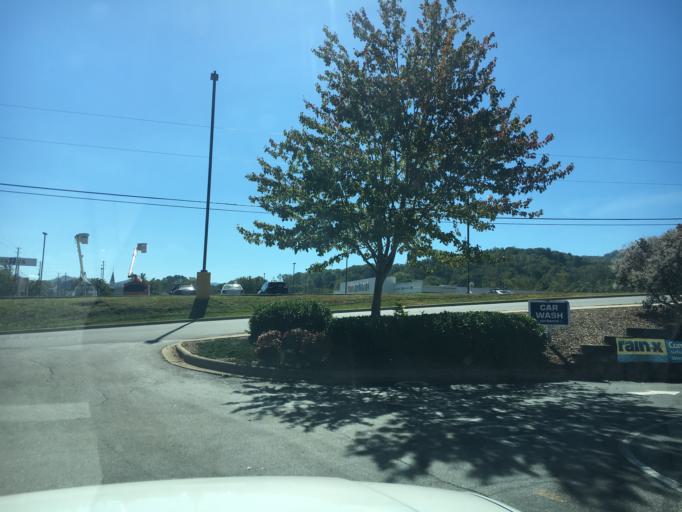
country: US
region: North Carolina
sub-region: Buncombe County
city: Bent Creek
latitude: 35.5297
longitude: -82.6066
